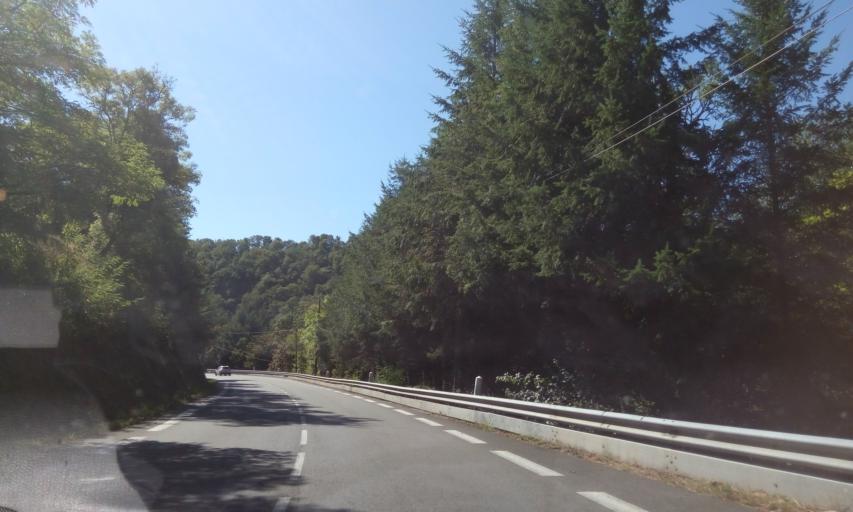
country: FR
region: Rhone-Alpes
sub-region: Departement du Rhone
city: Grandris
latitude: 45.9889
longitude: 4.5024
